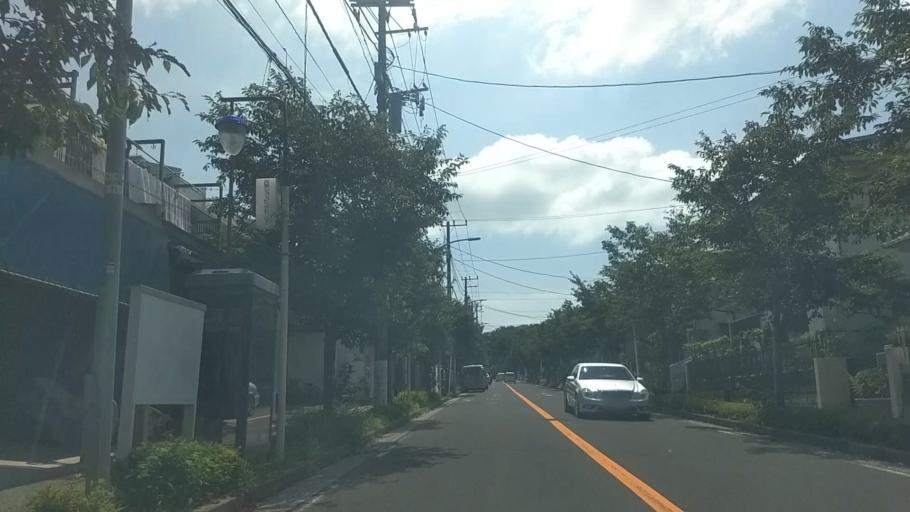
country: JP
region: Kanagawa
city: Zushi
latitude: 35.3479
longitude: 139.6276
